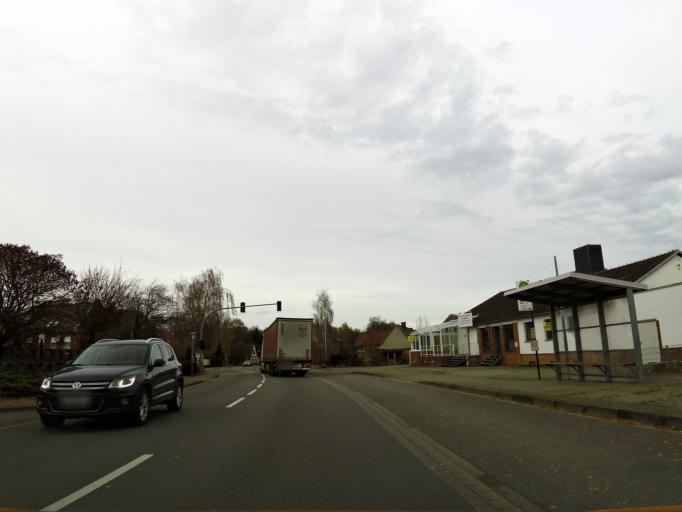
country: DE
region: Saxony-Anhalt
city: Pretzier
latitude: 52.7937
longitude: 11.2326
